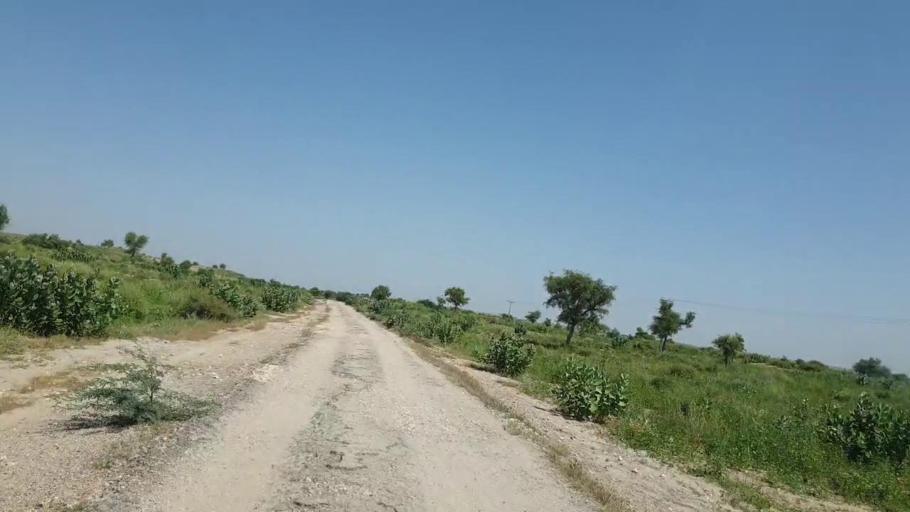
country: PK
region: Sindh
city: Islamkot
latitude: 25.1445
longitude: 70.4012
